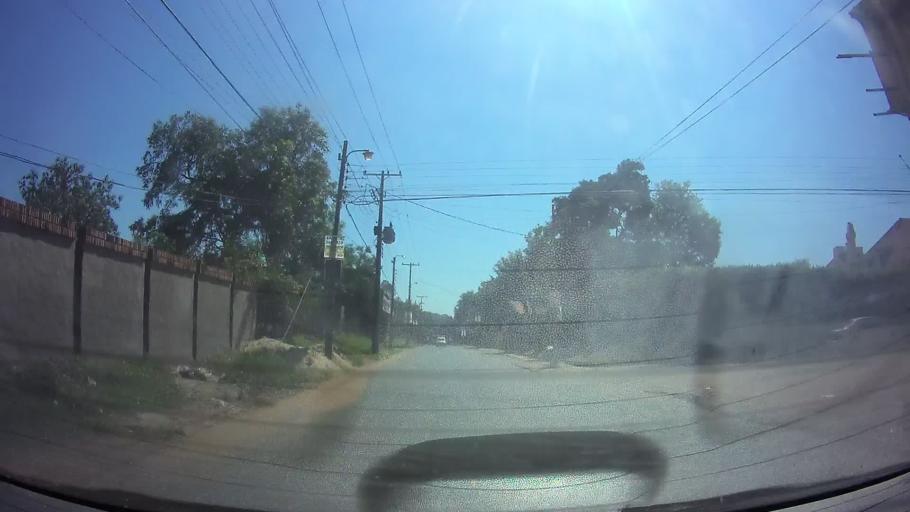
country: PY
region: Central
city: Fernando de la Mora
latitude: -25.3197
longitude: -57.5224
